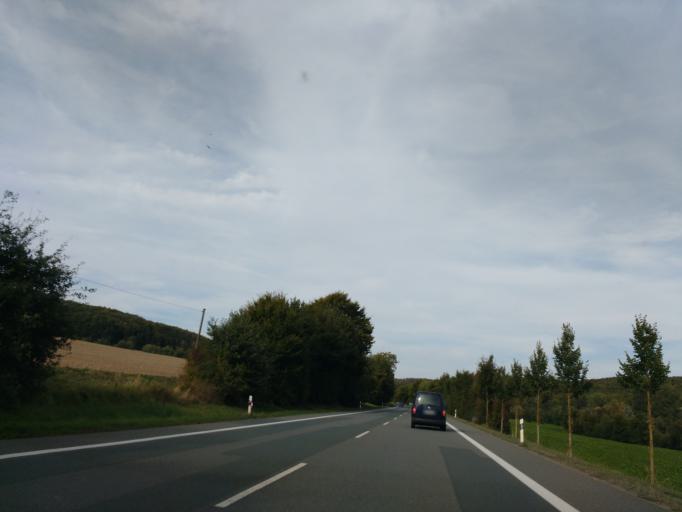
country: DE
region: North Rhine-Westphalia
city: Brakel
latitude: 51.7432
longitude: 9.1743
